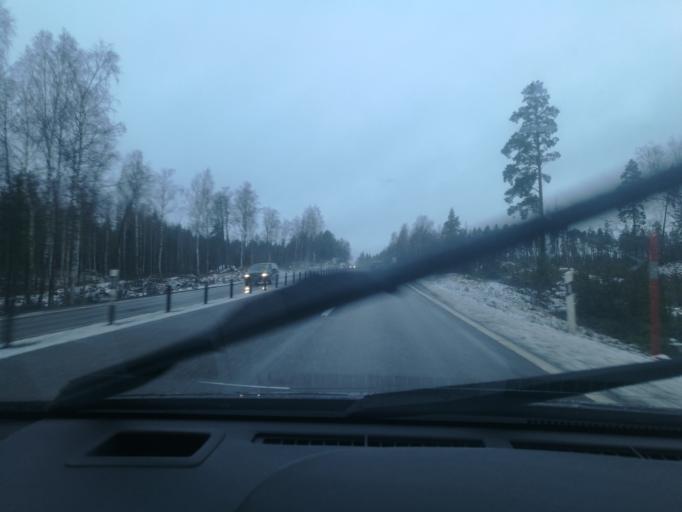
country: SE
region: OEstergoetland
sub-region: Norrkopings Kommun
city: Jursla
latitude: 58.7593
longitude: 16.1736
